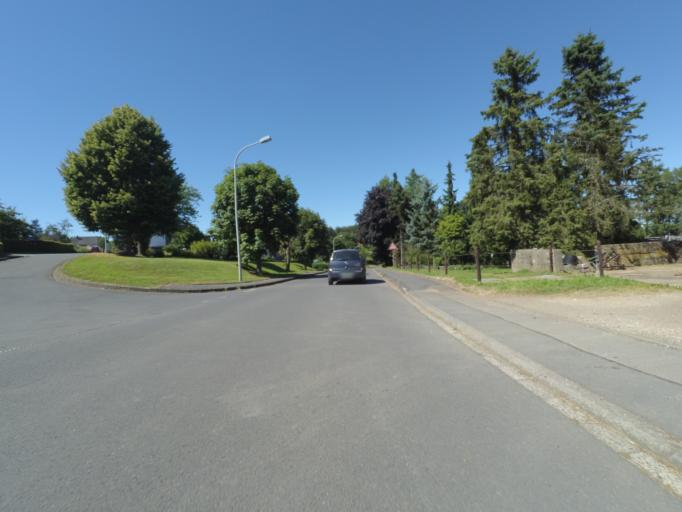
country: DE
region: Rheinland-Pfalz
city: Junkerath
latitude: 50.3356
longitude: 6.5703
